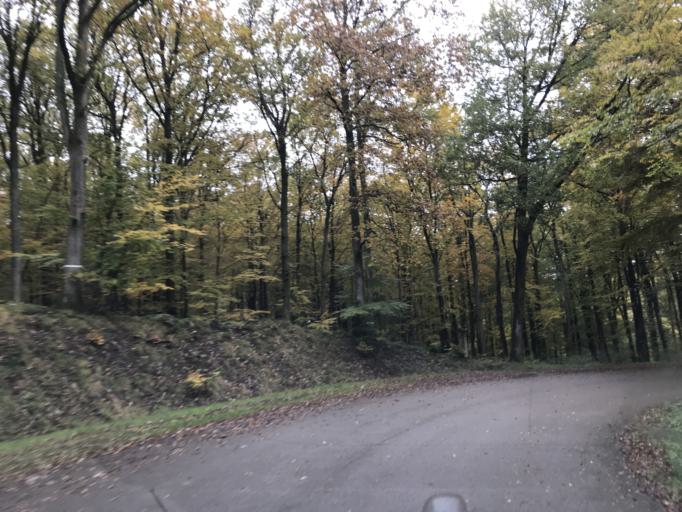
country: SE
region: Skane
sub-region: Klippans Kommun
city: Ljungbyhed
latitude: 56.0293
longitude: 13.2561
